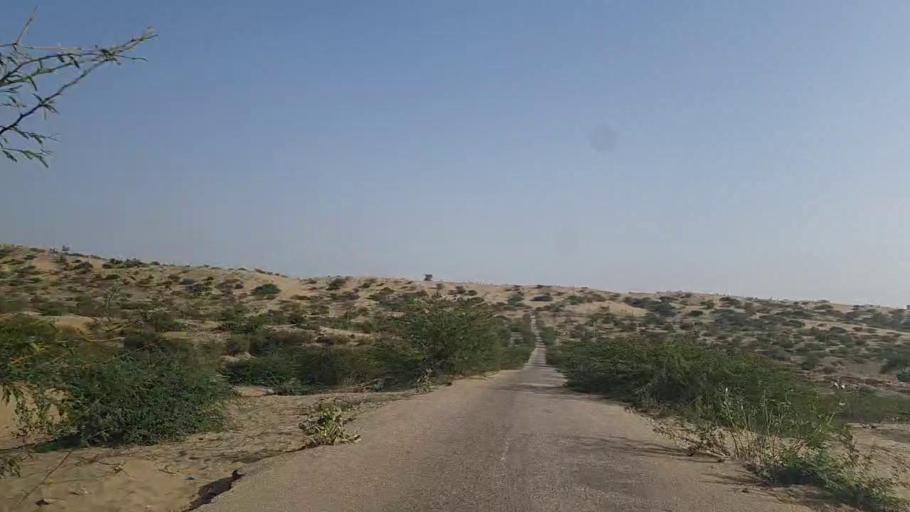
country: PK
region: Sindh
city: Naukot
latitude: 24.6220
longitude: 69.3705
